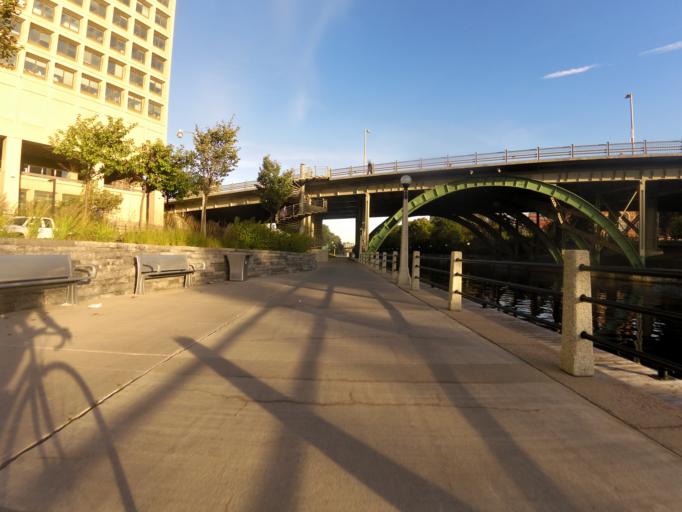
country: CA
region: Ontario
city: Ottawa
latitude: 45.4229
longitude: -75.6896
